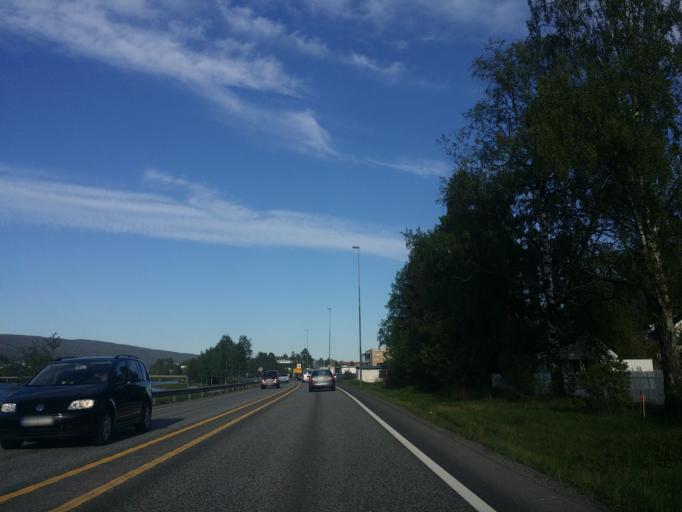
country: NO
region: Buskerud
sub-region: Nedre Eiker
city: Mjondalen
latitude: 59.7520
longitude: 10.0177
